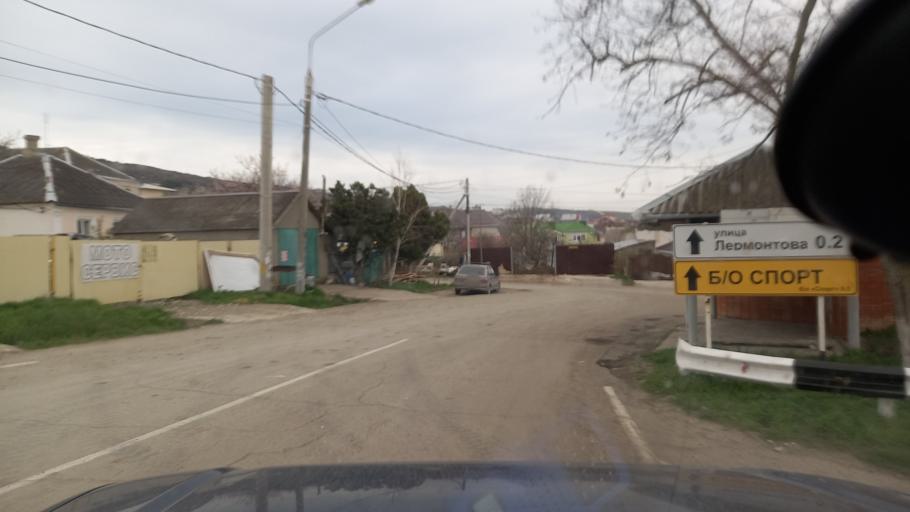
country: RU
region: Krasnodarskiy
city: Anapskaya
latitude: 44.8516
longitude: 37.3638
